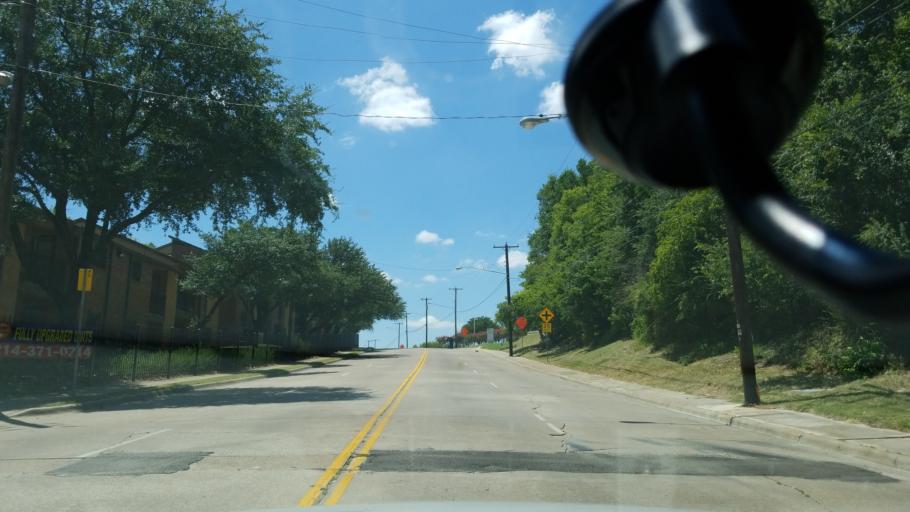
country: US
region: Texas
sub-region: Dallas County
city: Cockrell Hill
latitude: 32.7008
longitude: -96.8195
